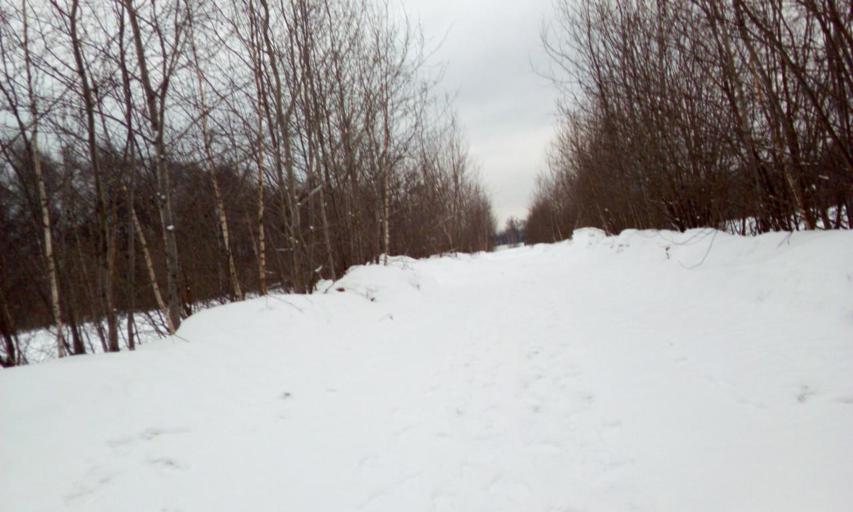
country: RU
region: Moskovskaya
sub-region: Leninskiy Rayon
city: Vnukovo
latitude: 55.6026
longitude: 37.3154
